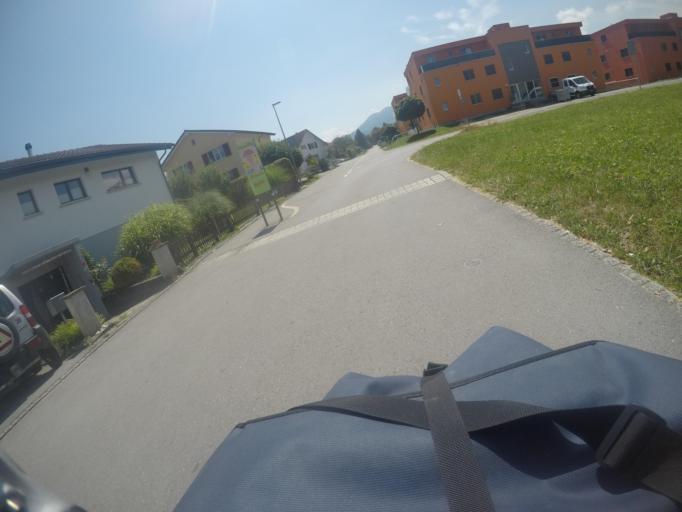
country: CH
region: Saint Gallen
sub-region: Wahlkreis Rheintal
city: Altstatten
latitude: 47.3750
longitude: 9.5589
